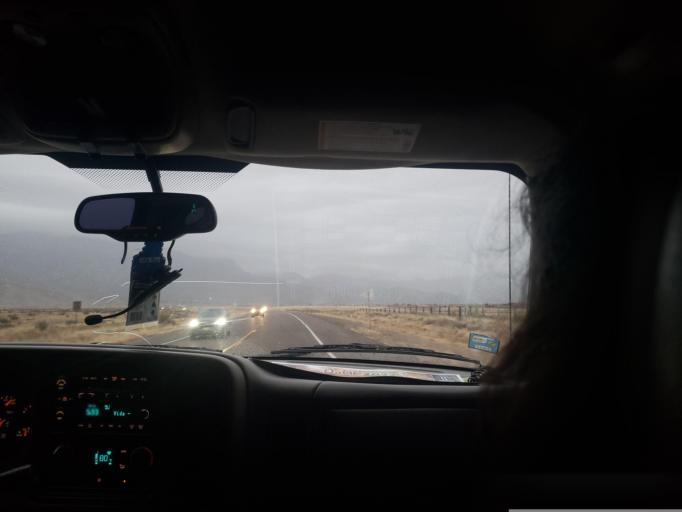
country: US
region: New Mexico
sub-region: Bernalillo County
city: Sandia Heights
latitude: 35.2018
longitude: -106.5518
